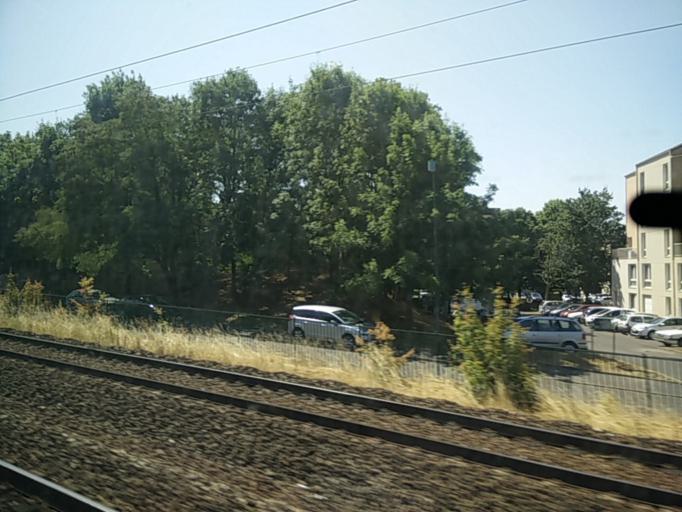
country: FR
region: Ile-de-France
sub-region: Departement de Seine-et-Marne
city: Roissy-en-Brie
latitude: 48.7978
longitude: 2.6442
